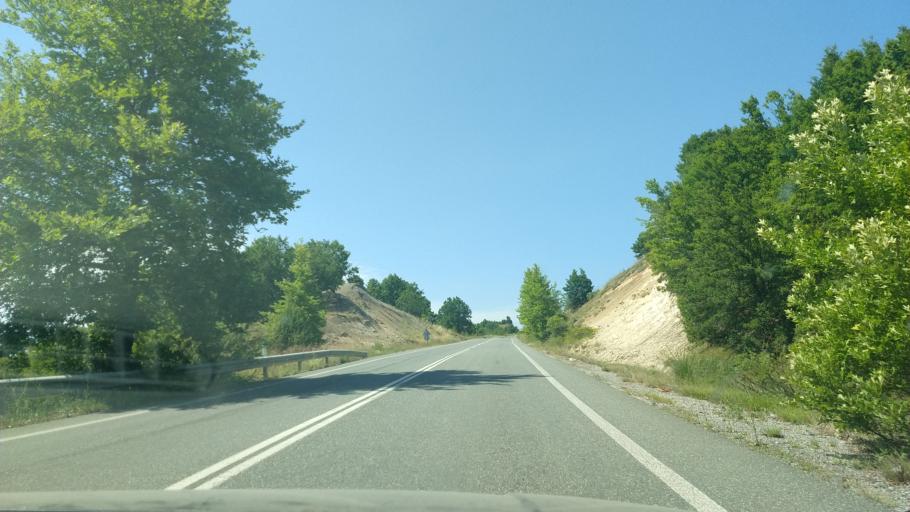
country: GR
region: West Macedonia
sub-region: Nomos Grevenon
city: Grevena
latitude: 40.0504
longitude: 21.4705
